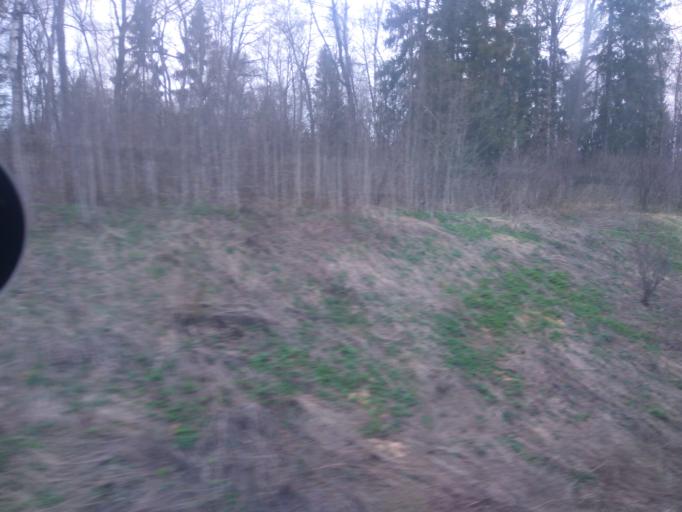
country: RU
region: Moskovskaya
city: Svatkovo
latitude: 56.3624
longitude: 38.2063
